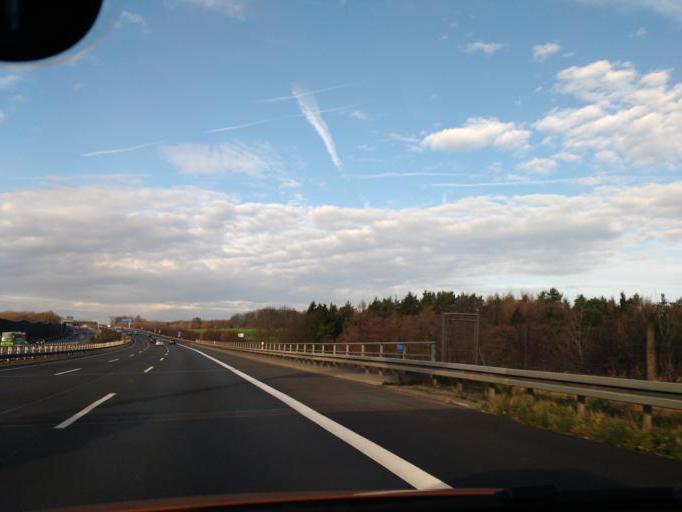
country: DE
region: Lower Saxony
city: Helmstedt
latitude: 52.2384
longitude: 11.0183
